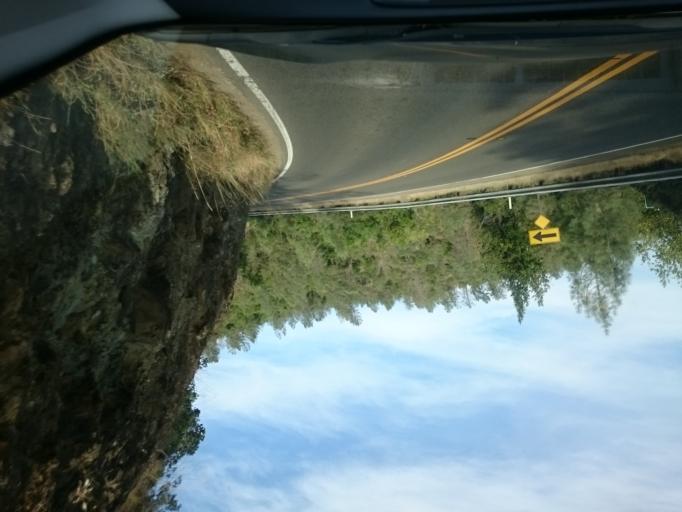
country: US
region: California
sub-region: Napa County
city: Yountville
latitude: 38.4802
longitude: -122.3726
